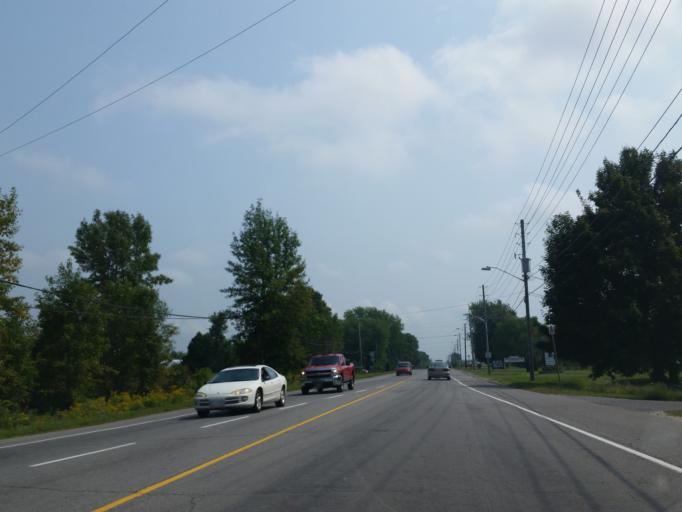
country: CA
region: Ontario
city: Brockville
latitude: 44.6089
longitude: -75.7291
